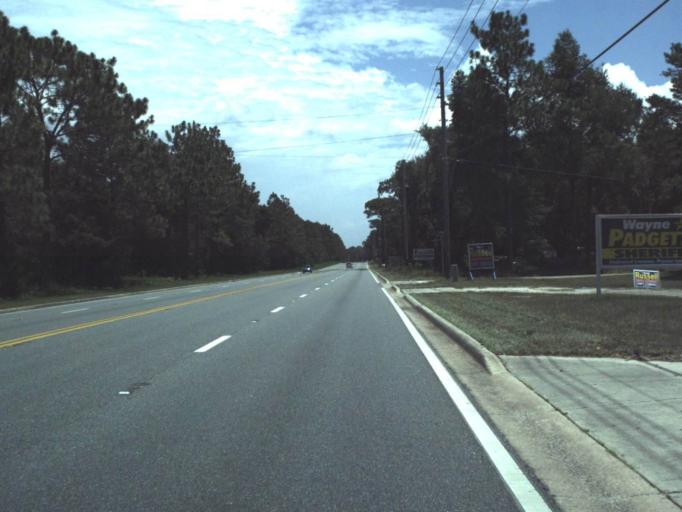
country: US
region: Florida
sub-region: Taylor County
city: Perry
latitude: 30.1005
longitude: -83.5546
